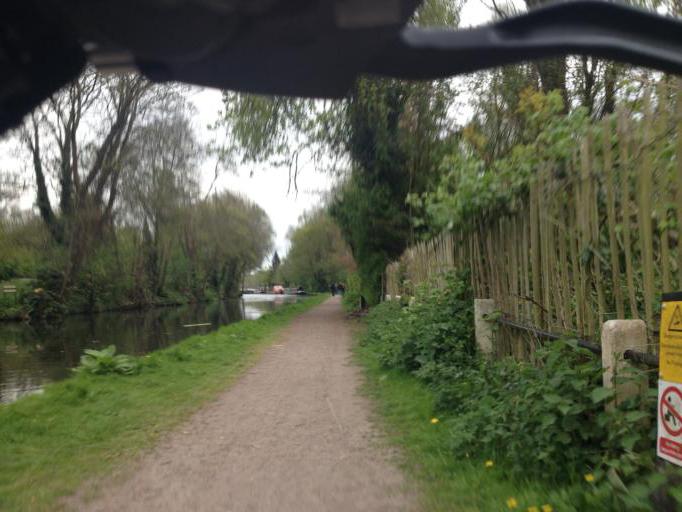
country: GB
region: England
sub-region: Greater London
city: Harefield
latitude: 51.6045
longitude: -0.4972
